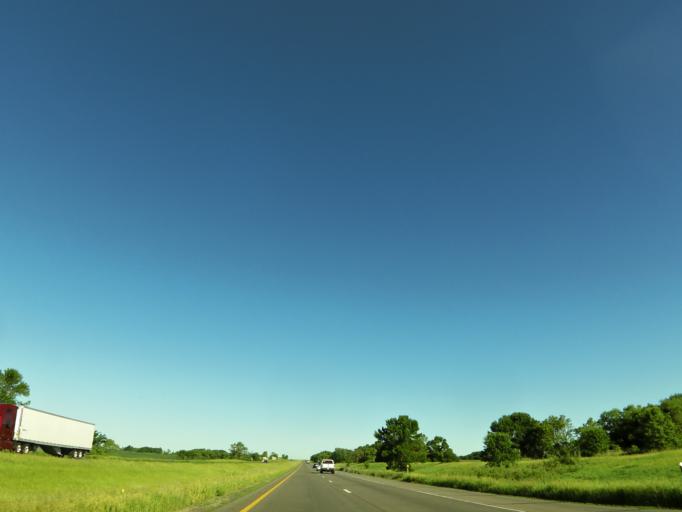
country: US
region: Minnesota
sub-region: Stearns County
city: Sauk Centre
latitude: 45.7021
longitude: -94.8967
